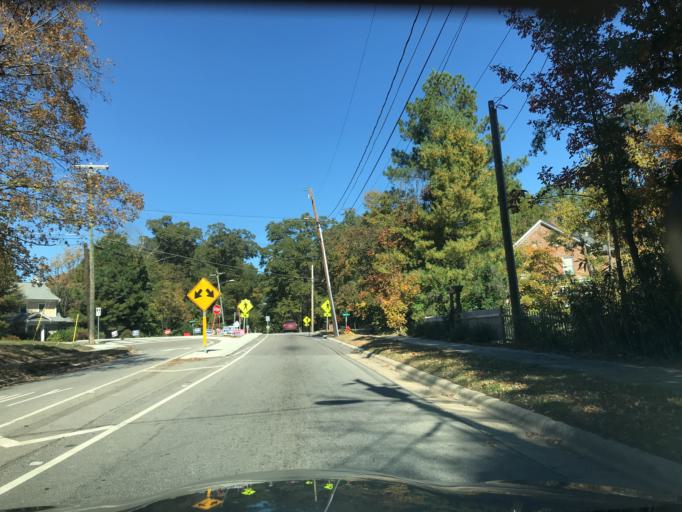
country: US
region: North Carolina
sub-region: Durham County
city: Durham
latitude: 36.0093
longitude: -78.8919
